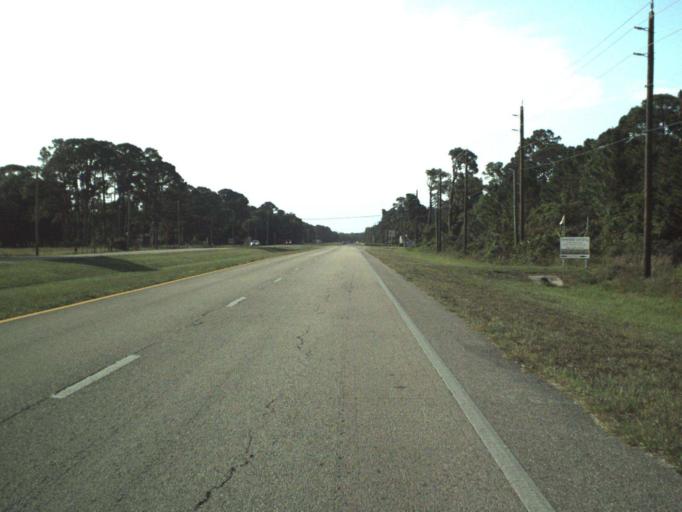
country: US
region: Florida
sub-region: Volusia County
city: Oak Hill
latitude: 28.8802
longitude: -80.8544
